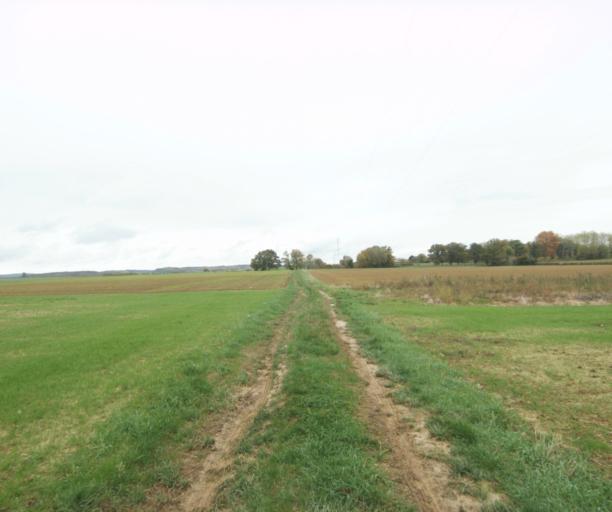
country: FR
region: Bourgogne
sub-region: Departement de Saone-et-Loire
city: Saint-Martin-Belle-Roche
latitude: 46.4603
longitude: 4.8664
